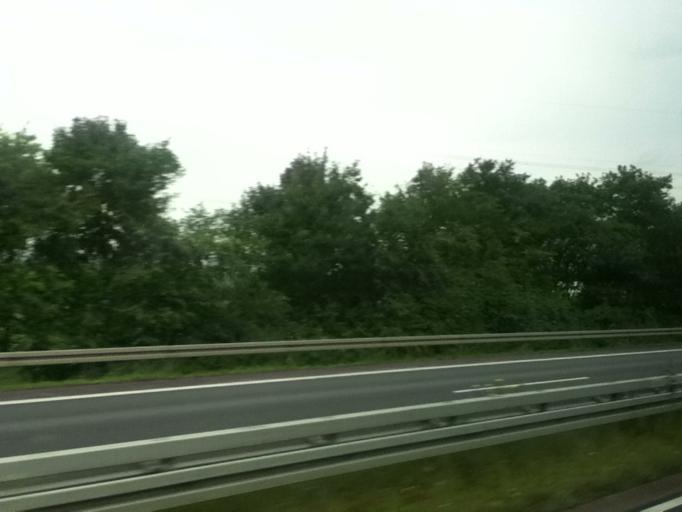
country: DE
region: Hesse
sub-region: Regierungsbezirk Giessen
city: Heuchelheim
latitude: 50.5758
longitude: 8.6458
